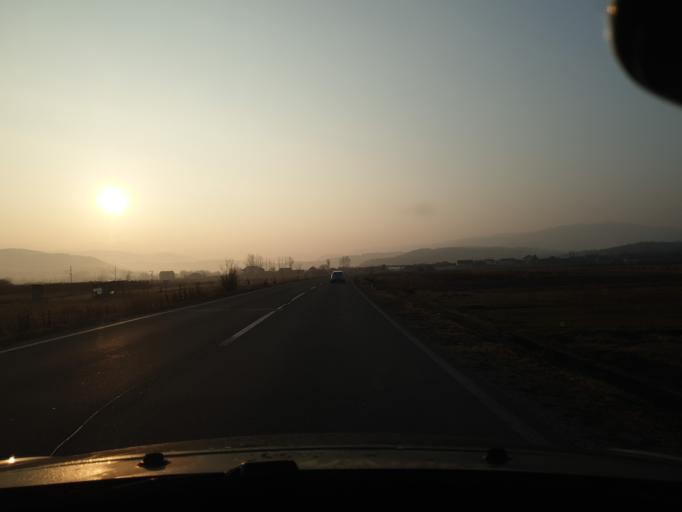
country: RS
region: Central Serbia
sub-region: Jablanicki Okrug
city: Leskovac
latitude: 42.9327
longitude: 22.0127
